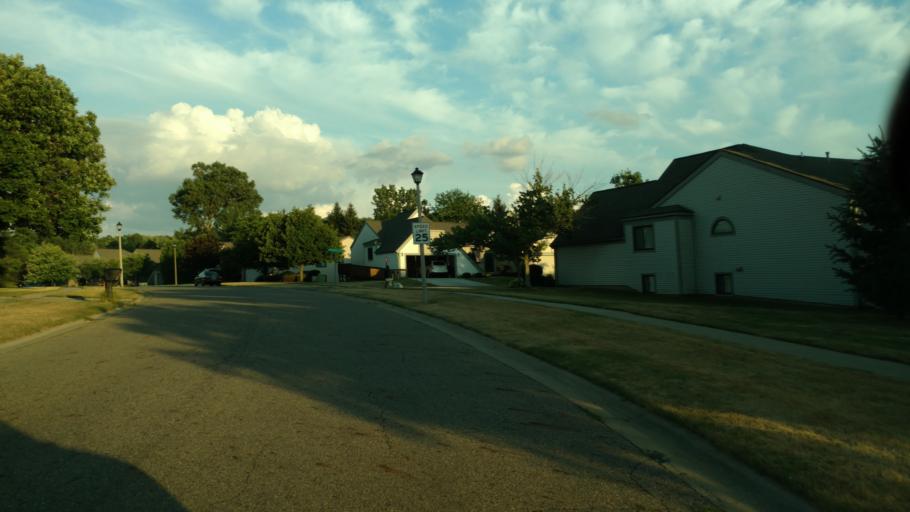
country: US
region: Michigan
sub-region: Eaton County
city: Waverly
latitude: 42.7215
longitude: -84.6194
